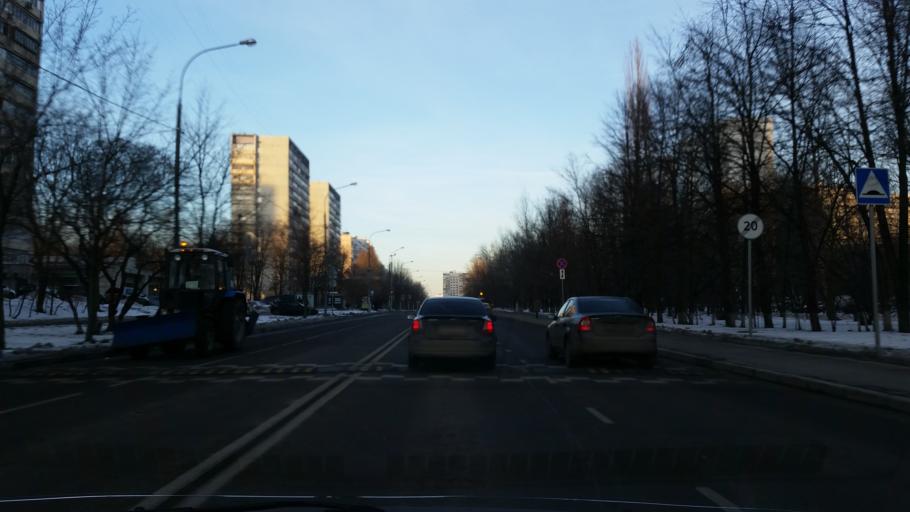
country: RU
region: Moscow
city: Nagornyy
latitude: 55.6268
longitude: 37.6109
